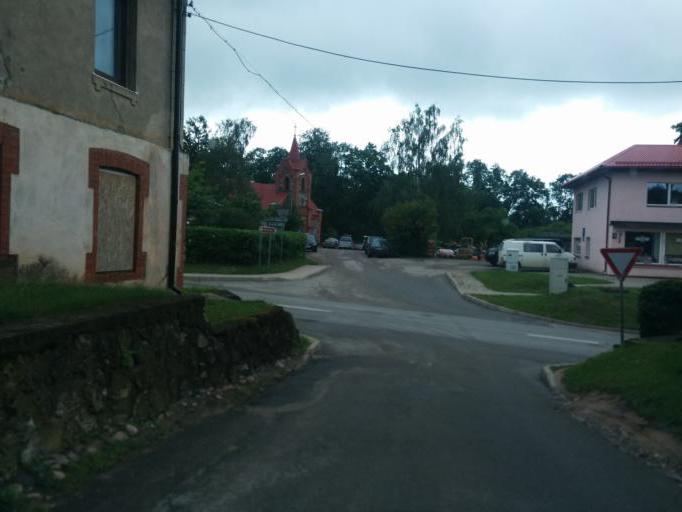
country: LV
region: Smiltene
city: Smiltene
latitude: 57.4273
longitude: 25.8951
